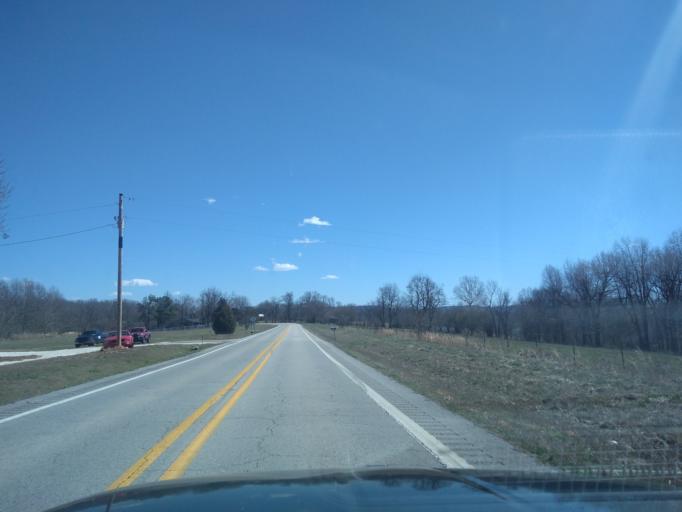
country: US
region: Arkansas
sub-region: Washington County
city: Farmington
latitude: 36.0810
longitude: -94.3102
